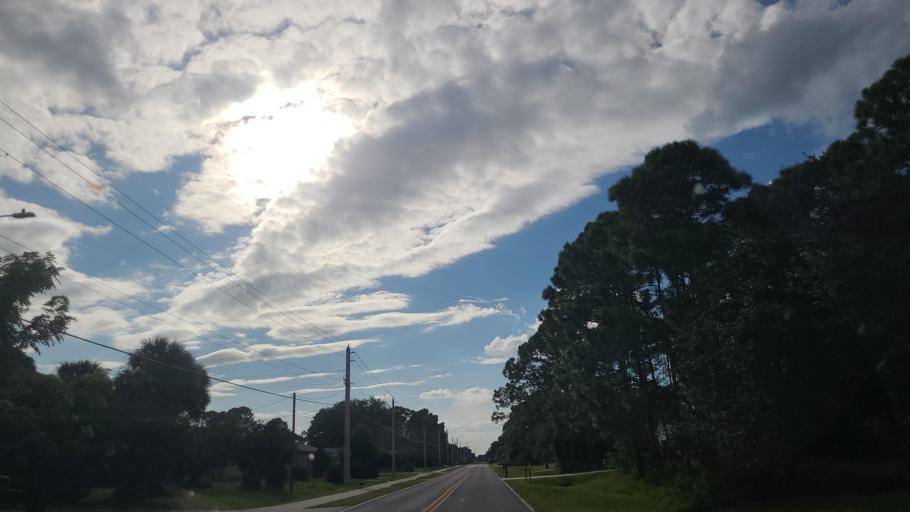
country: US
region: Florida
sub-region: Brevard County
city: West Melbourne
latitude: 28.0117
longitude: -80.6660
